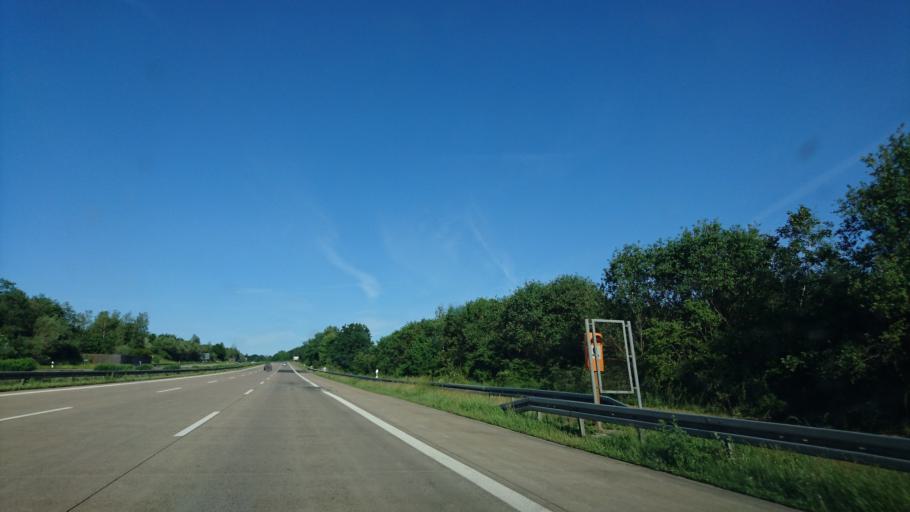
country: DE
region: Saxony
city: Frankenberg
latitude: 50.9139
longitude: 13.0077
